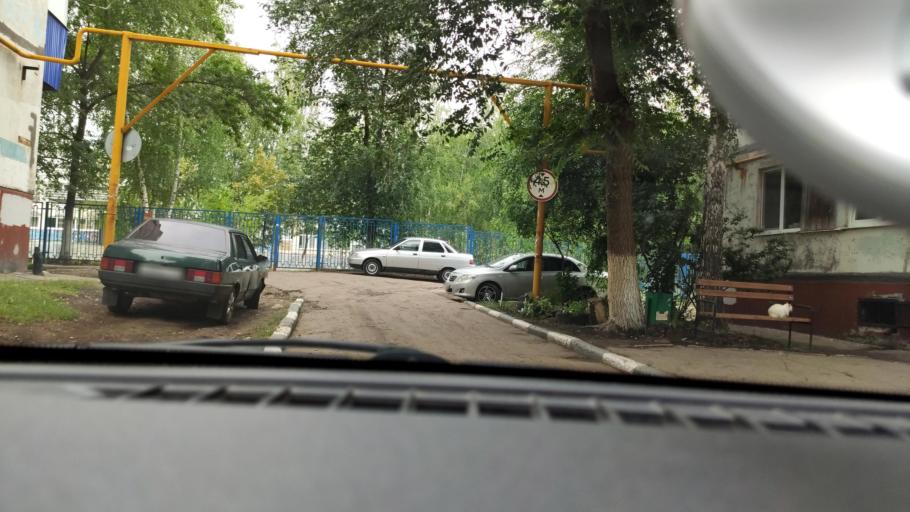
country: RU
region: Samara
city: Novokuybyshevsk
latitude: 53.0927
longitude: 49.9905
